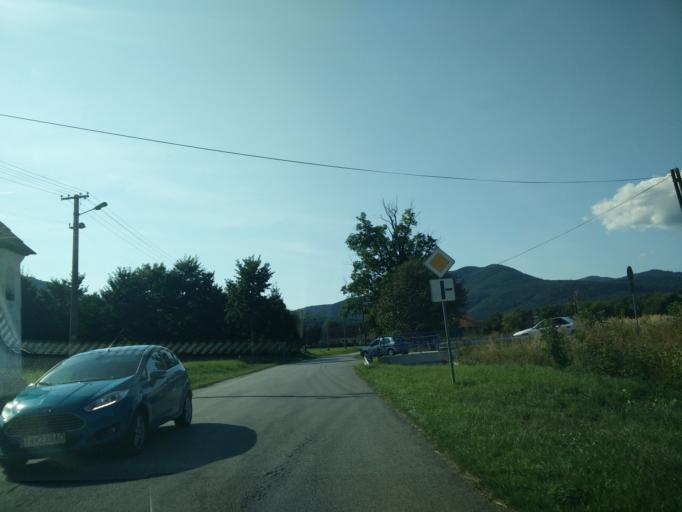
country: SK
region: Zilinsky
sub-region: Okres Martin
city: Martin
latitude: 48.9696
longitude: 18.8127
